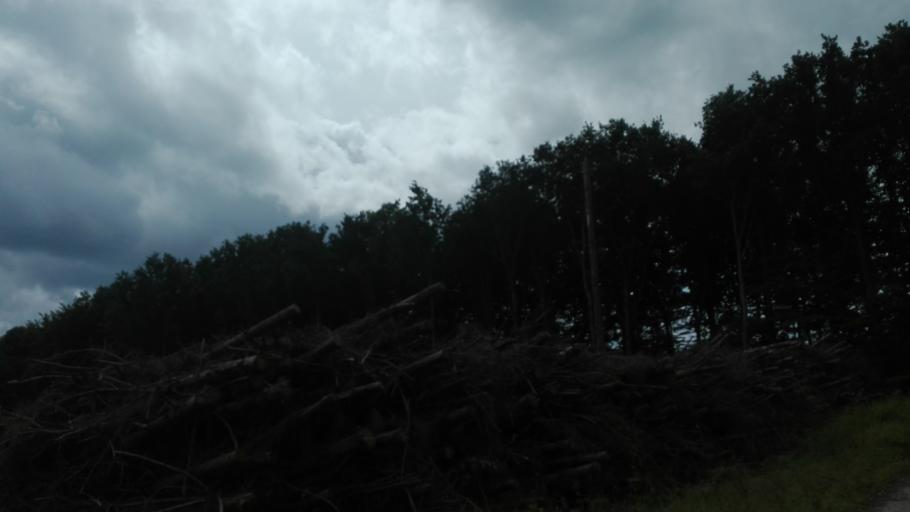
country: DK
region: Central Jutland
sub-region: Arhus Kommune
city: Logten
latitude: 56.2705
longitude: 10.3412
